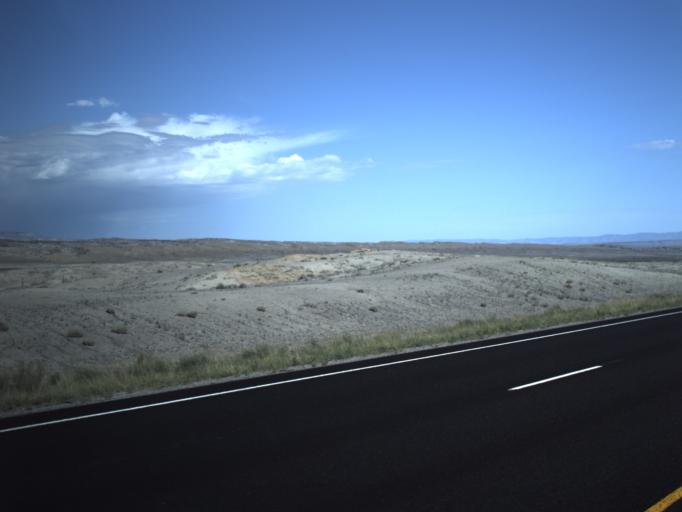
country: US
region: Utah
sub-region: Carbon County
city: East Carbon City
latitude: 39.2092
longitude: -110.3386
